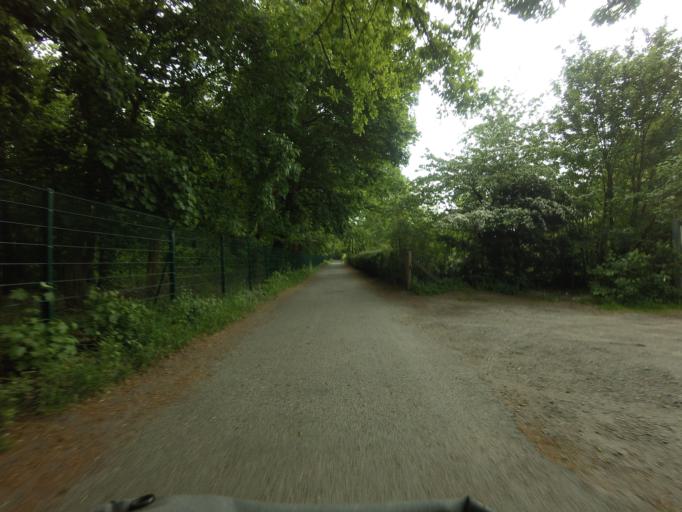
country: DE
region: Lower Saxony
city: Braunschweig
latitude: 52.2949
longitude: 10.5338
